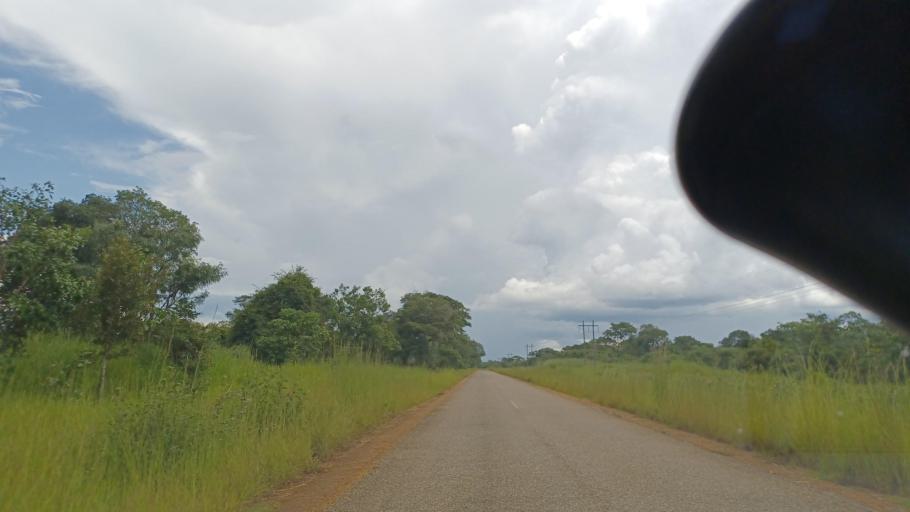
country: ZM
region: North-Western
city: Kasempa
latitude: -13.1465
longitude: 25.8776
